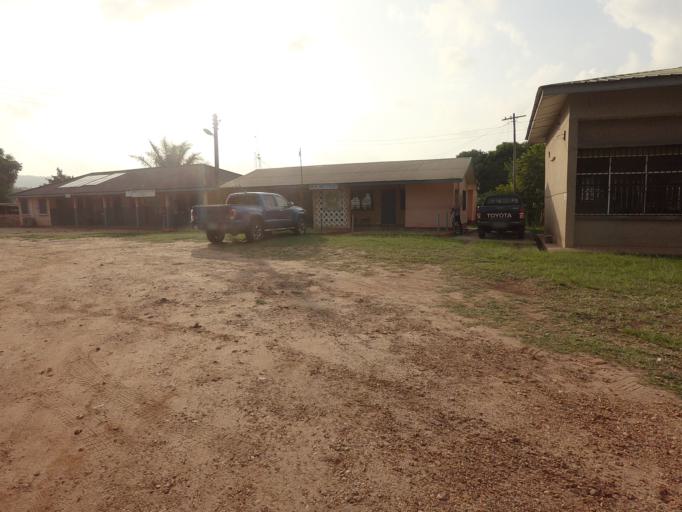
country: GH
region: Volta
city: Ho
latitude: 6.6091
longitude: 0.4731
